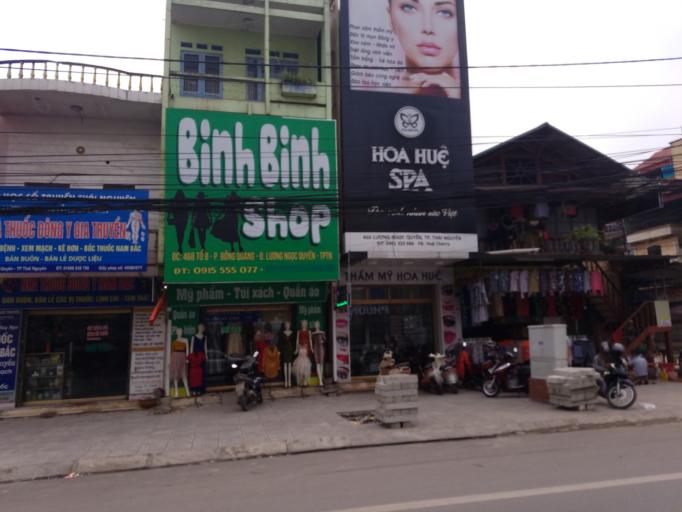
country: VN
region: Thai Nguyen
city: Thanh Pho Thai Nguyen
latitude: 21.5855
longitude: 105.8325
